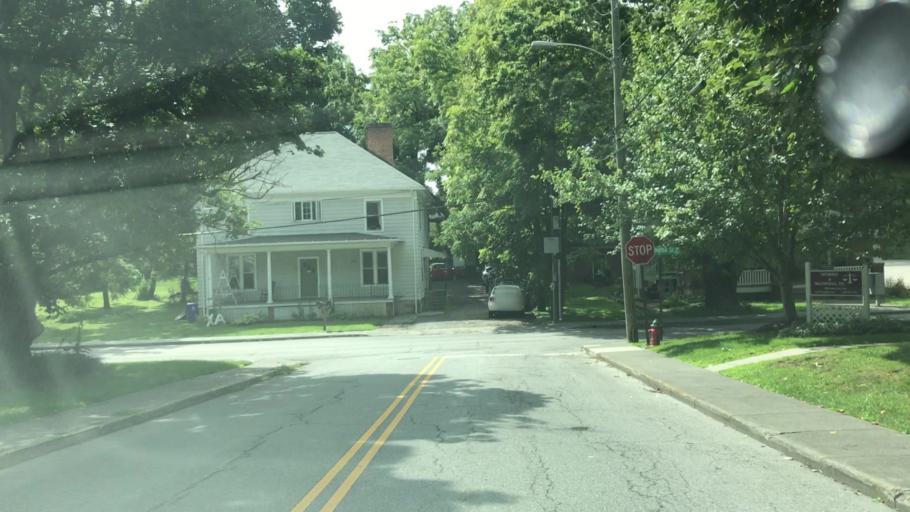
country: US
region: Virginia
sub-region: Montgomery County
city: Blacksburg
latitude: 37.2266
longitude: -80.4151
